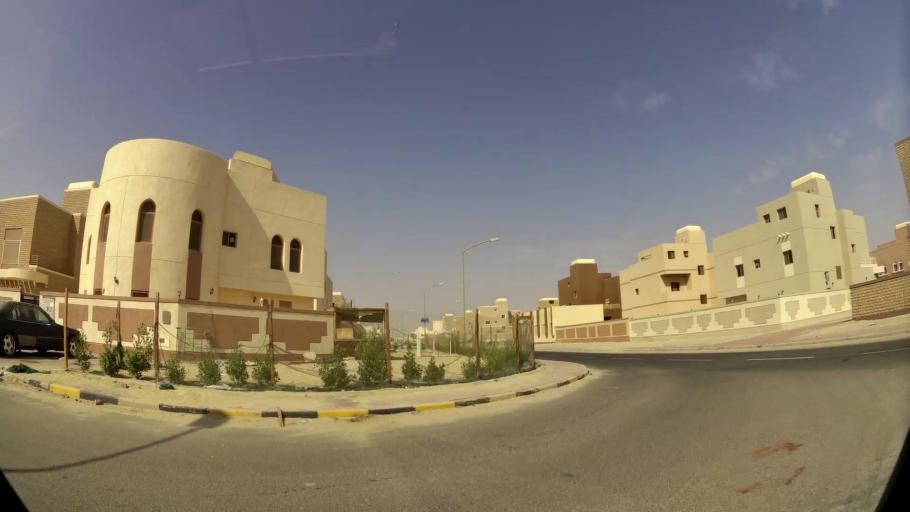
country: KW
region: Al Ahmadi
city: Al Wafrah
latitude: 28.8044
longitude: 48.0663
